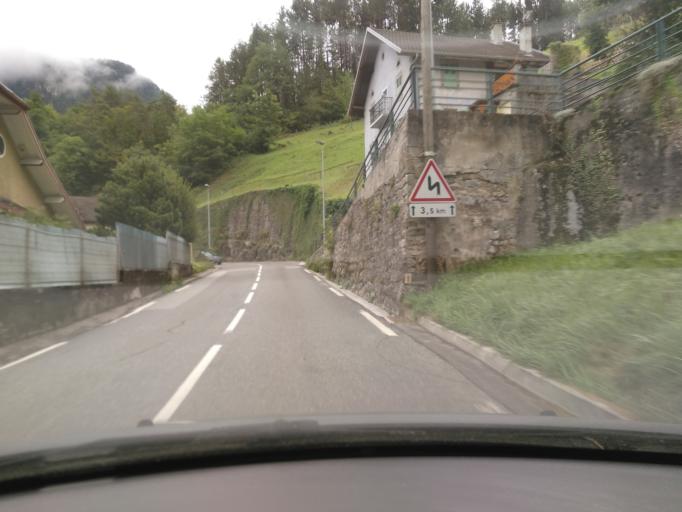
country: FR
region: Rhone-Alpes
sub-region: Departement de la Haute-Savoie
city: Bonneville
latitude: 46.0540
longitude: 6.3725
